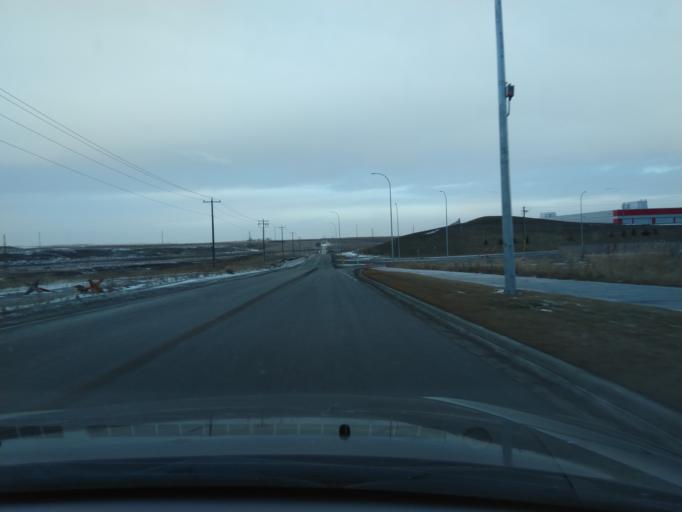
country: CA
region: Alberta
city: Calgary
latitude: 51.1641
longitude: -114.0248
